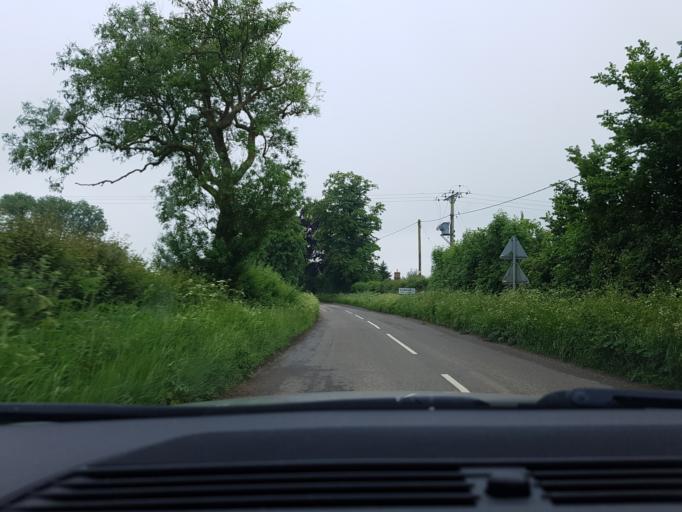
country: GB
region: England
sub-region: Buckinghamshire
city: Steeple Claydon
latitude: 51.9355
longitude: -0.9382
